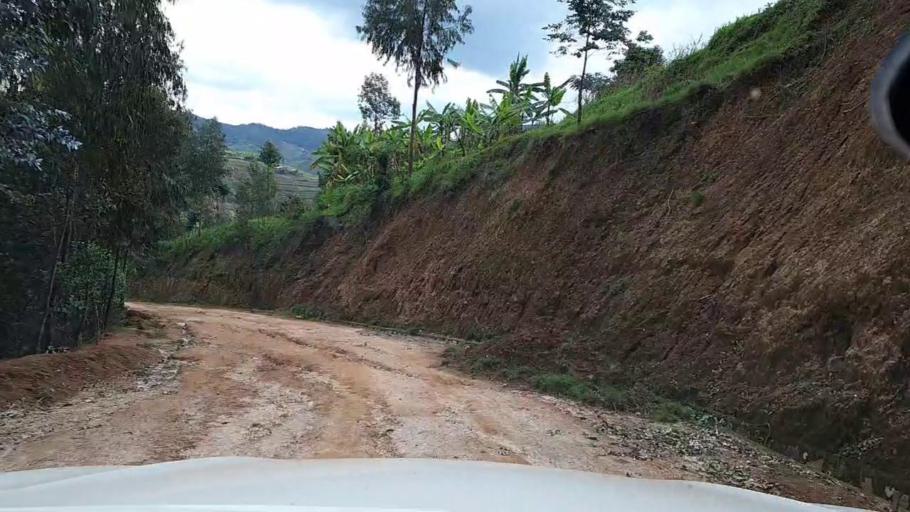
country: RW
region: Southern Province
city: Nzega
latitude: -2.6946
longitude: 29.4429
